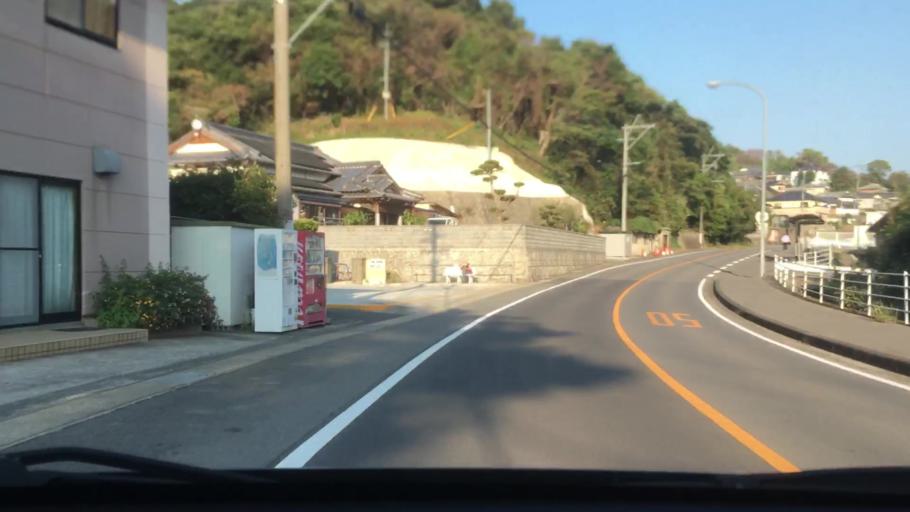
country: JP
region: Nagasaki
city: Sasebo
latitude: 33.0344
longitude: 129.6075
